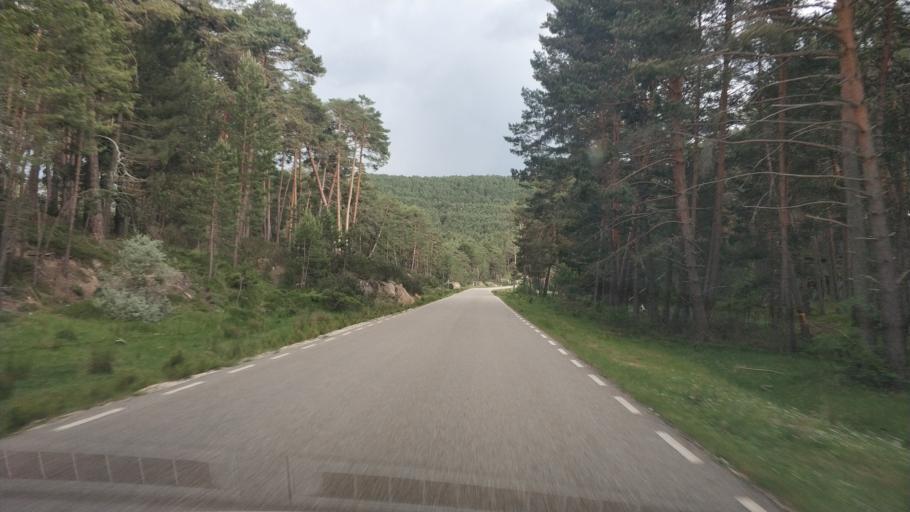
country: ES
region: Castille and Leon
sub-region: Provincia de Soria
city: San Leonardo de Yague
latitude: 41.8548
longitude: -3.0721
